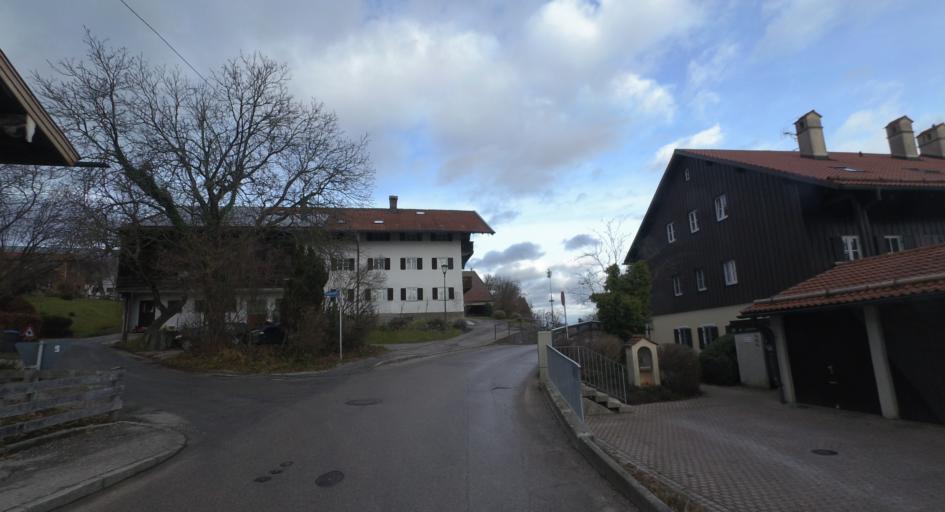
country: DE
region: Bavaria
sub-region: Upper Bavaria
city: Prien am Chiemsee
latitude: 47.8500
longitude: 12.3403
